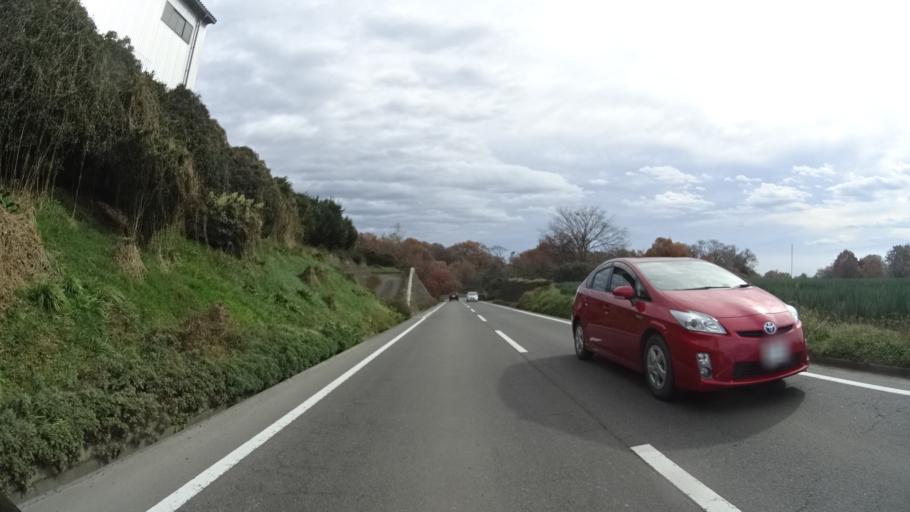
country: JP
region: Gunma
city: Shibukawa
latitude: 36.4945
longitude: 139.1075
